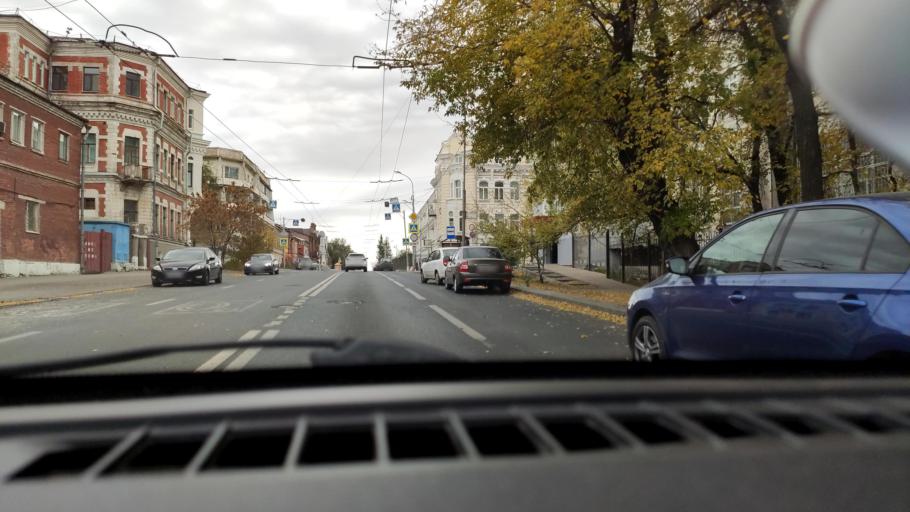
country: RU
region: Samara
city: Rozhdestveno
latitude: 53.1840
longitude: 50.0827
